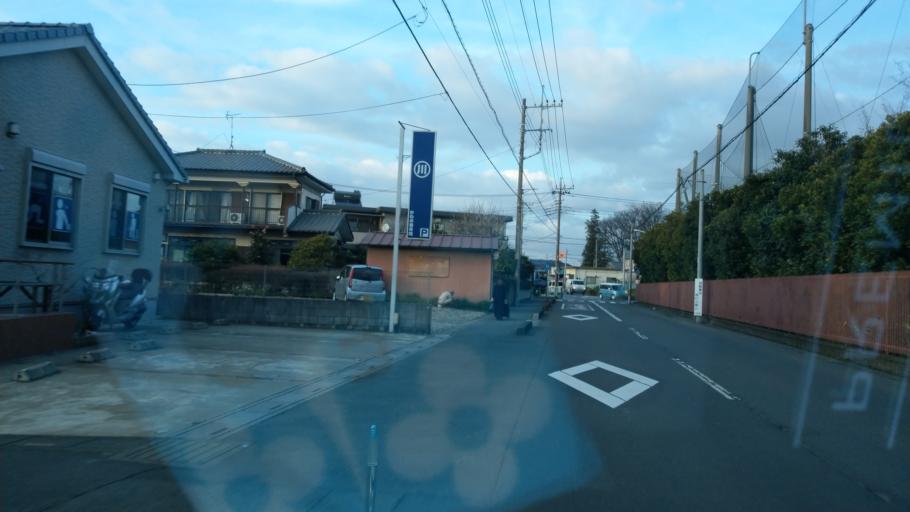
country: JP
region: Saitama
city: Yono
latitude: 35.8956
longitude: 139.5880
